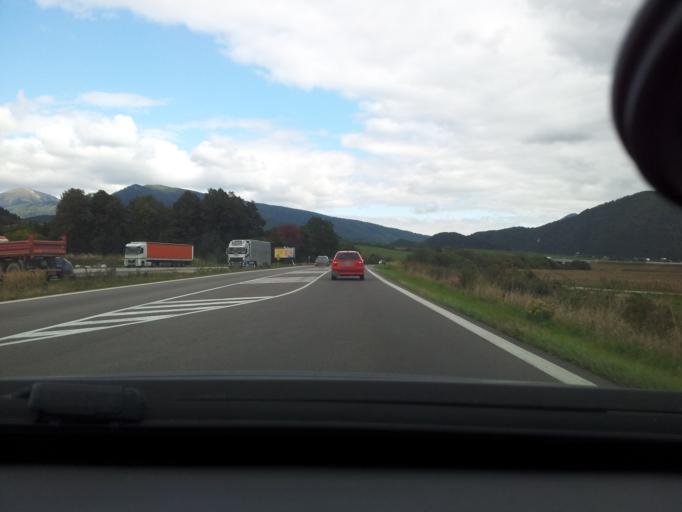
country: SK
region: Zilinsky
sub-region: Okres Zilina
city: Terchova
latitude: 49.1290
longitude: 19.0611
